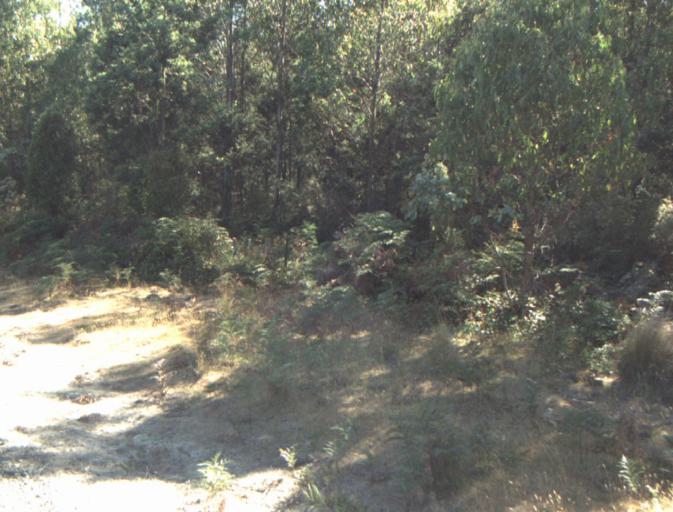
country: AU
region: Tasmania
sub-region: Dorset
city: Scottsdale
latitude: -41.2705
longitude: 147.3764
